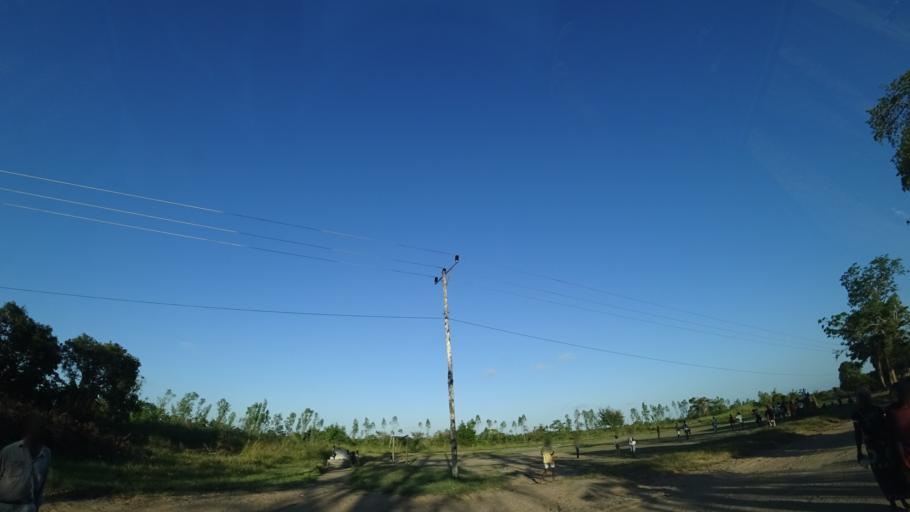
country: MZ
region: Sofala
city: Dondo
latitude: -19.3878
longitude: 34.7082
